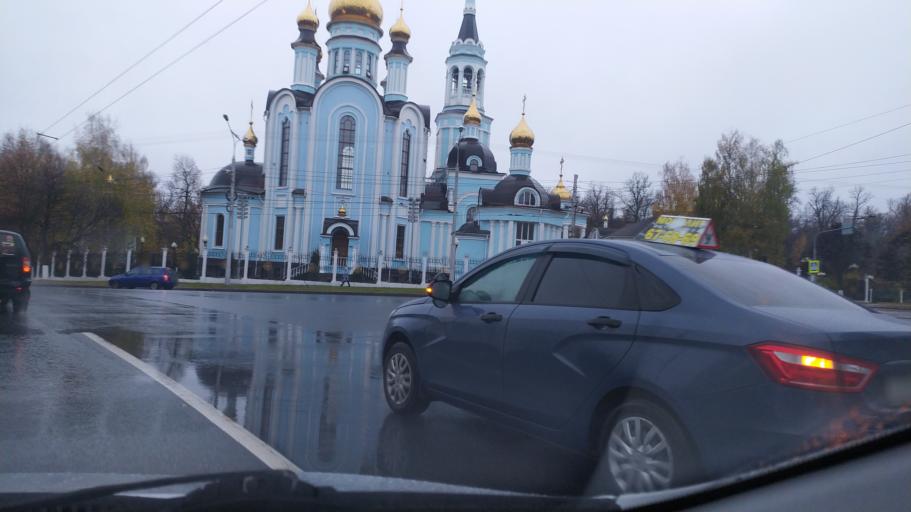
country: RU
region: Chuvashia
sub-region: Cheboksarskiy Rayon
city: Cheboksary
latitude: 56.1412
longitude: 47.1861
